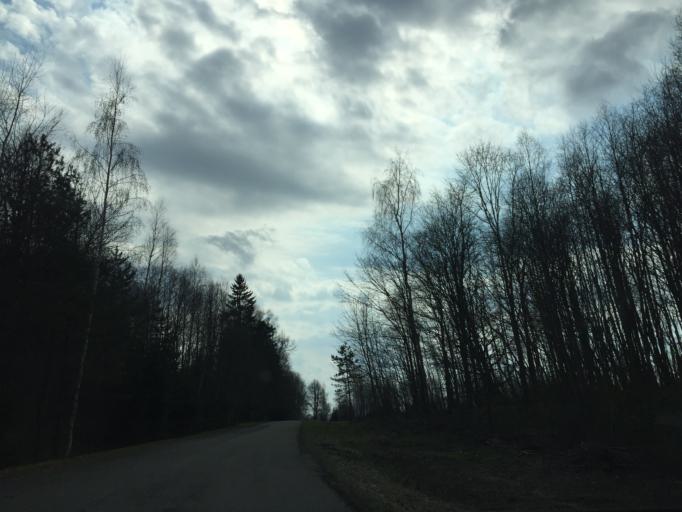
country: LV
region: Aluksnes Rajons
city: Aluksne
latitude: 57.5531
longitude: 26.9010
